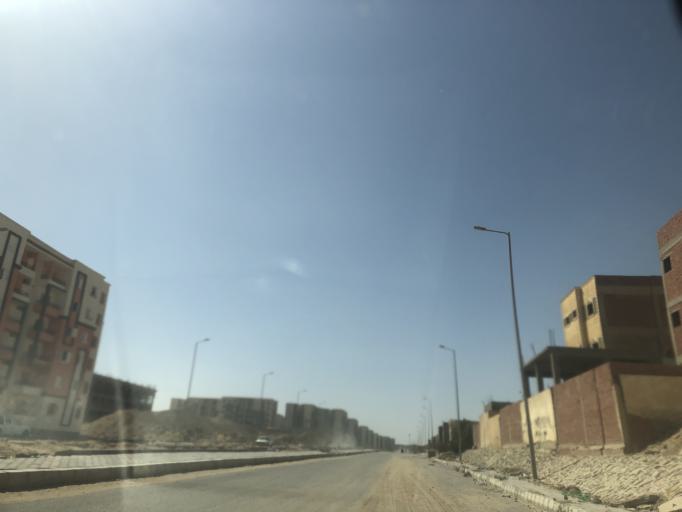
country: EG
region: Al Jizah
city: Madinat Sittah Uktubar
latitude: 29.9276
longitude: 30.9940
